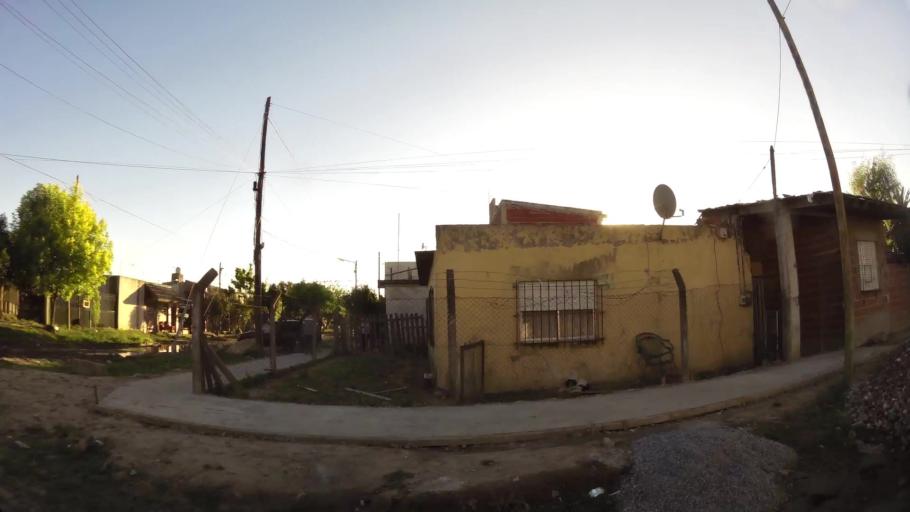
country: AR
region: Buenos Aires
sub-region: Partido de Almirante Brown
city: Adrogue
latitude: -34.7746
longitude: -58.3335
